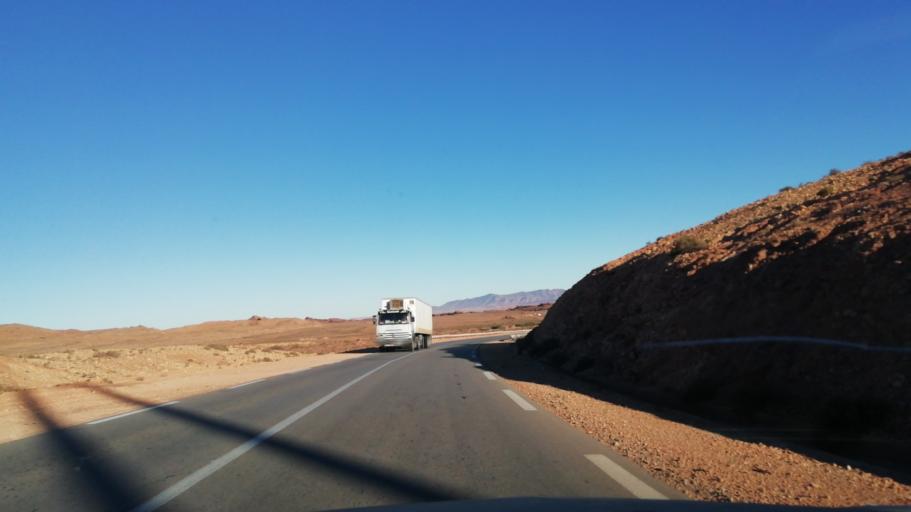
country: DZ
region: El Bayadh
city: El Abiodh Sidi Cheikh
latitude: 33.1749
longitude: 0.4484
